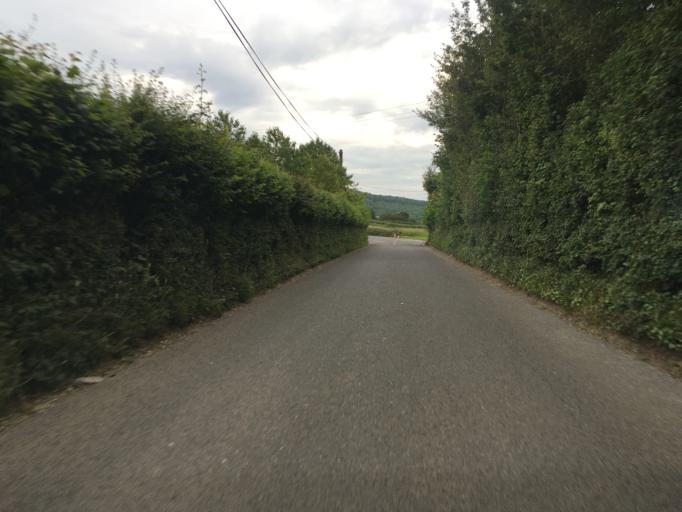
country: GB
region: England
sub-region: North Somerset
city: Long Ashton
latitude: 51.4267
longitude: -2.7022
